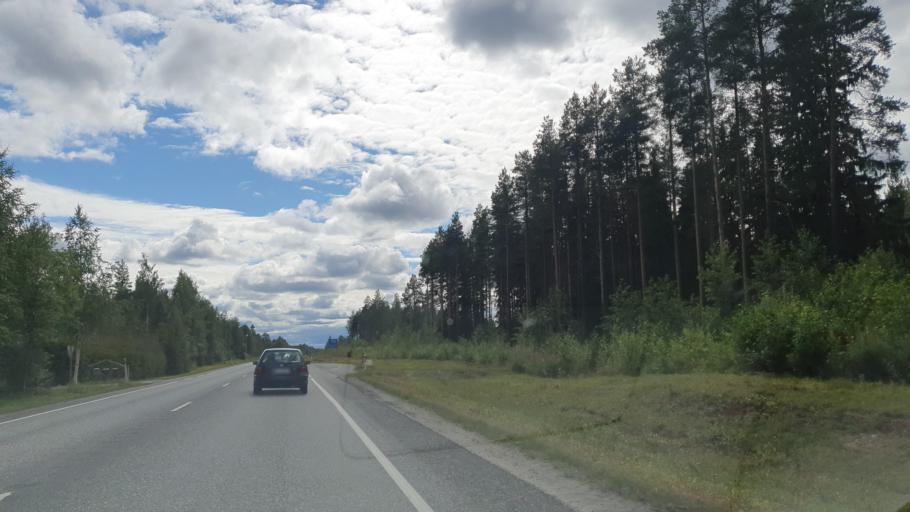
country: FI
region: Kainuu
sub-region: Kajaani
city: Kajaani
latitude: 64.1641
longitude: 27.5258
